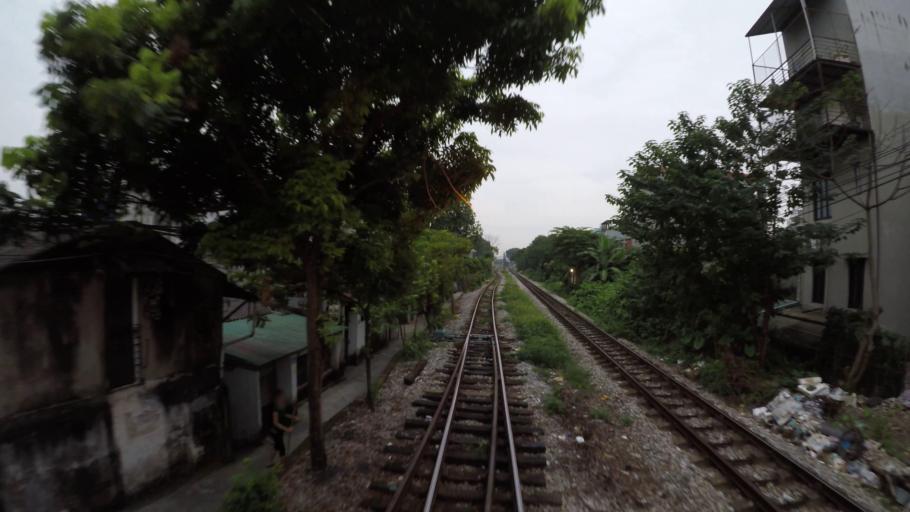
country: VN
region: Ha Noi
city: Trau Quy
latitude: 21.0367
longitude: 105.8999
